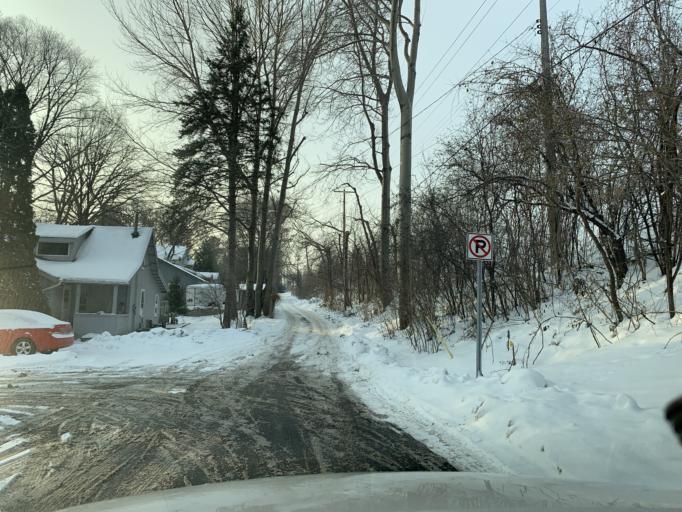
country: US
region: Minnesota
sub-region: Hennepin County
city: Edina
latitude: 44.9186
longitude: -93.3533
